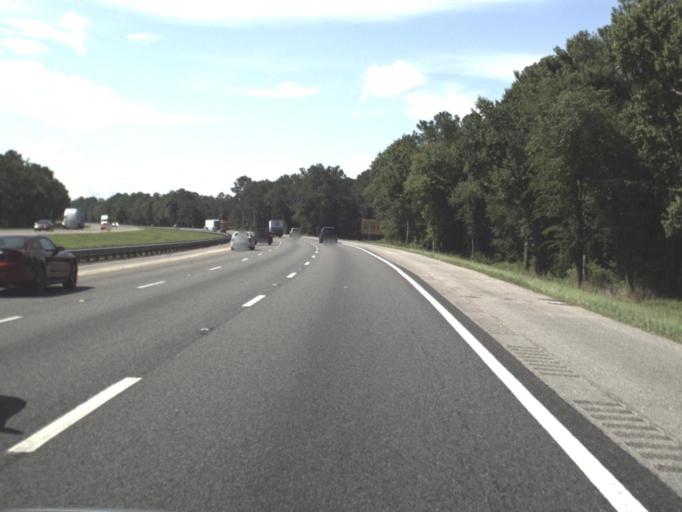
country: US
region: Florida
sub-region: Saint Johns County
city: Fruit Cove
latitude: 30.0463
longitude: -81.4971
